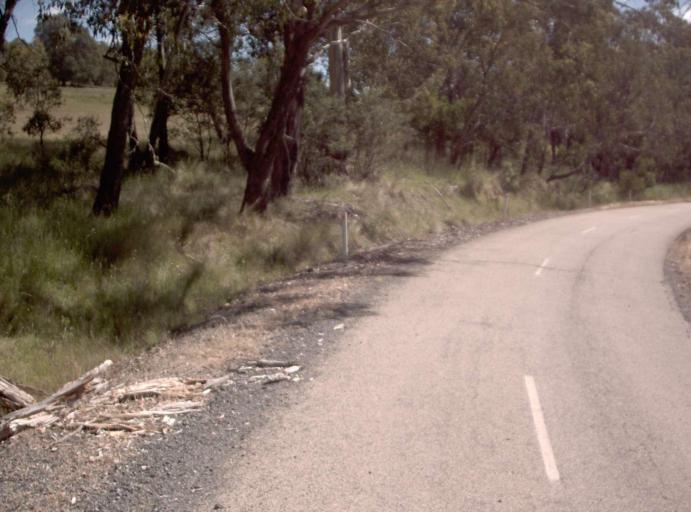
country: AU
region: New South Wales
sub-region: Bombala
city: Bombala
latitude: -37.0614
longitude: 148.7999
